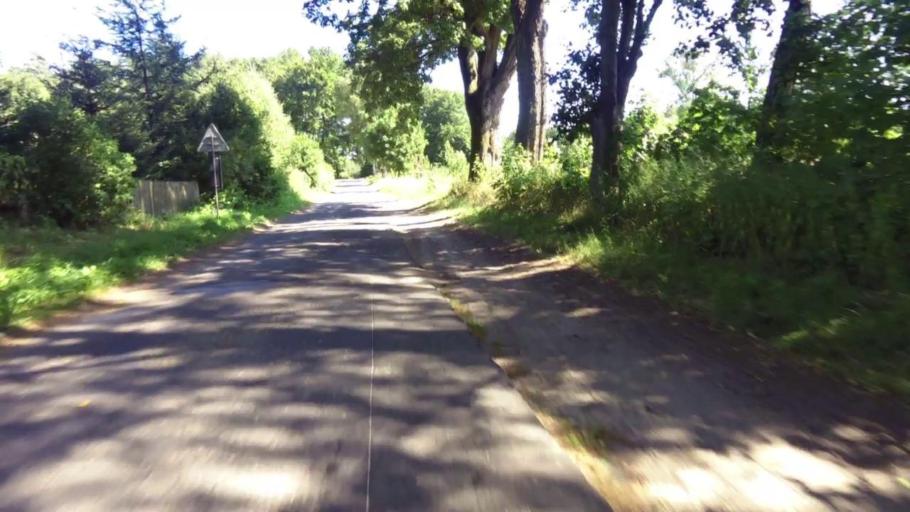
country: PL
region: West Pomeranian Voivodeship
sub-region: Powiat drawski
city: Zlocieniec
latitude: 53.5292
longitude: 16.0804
